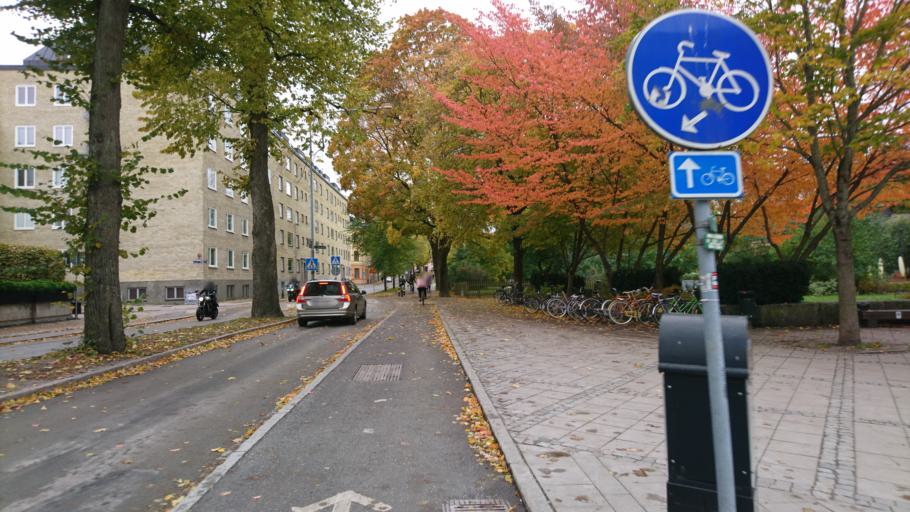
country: SE
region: Uppsala
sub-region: Uppsala Kommun
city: Uppsala
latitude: 59.8605
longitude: 17.6282
